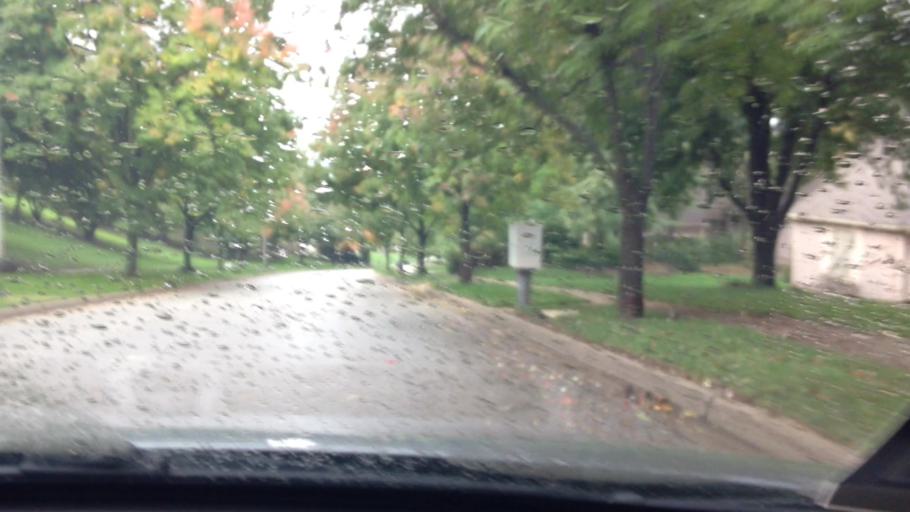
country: US
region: Missouri
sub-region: Platte County
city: Riverside
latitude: 39.1719
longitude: -94.5981
